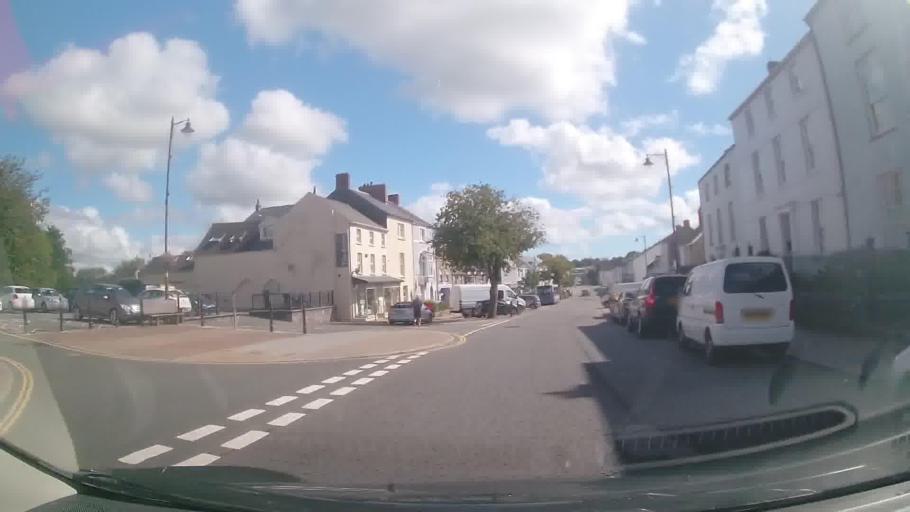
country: GB
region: Wales
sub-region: Pembrokeshire
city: Pembroke
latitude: 51.6745
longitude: -4.9111
